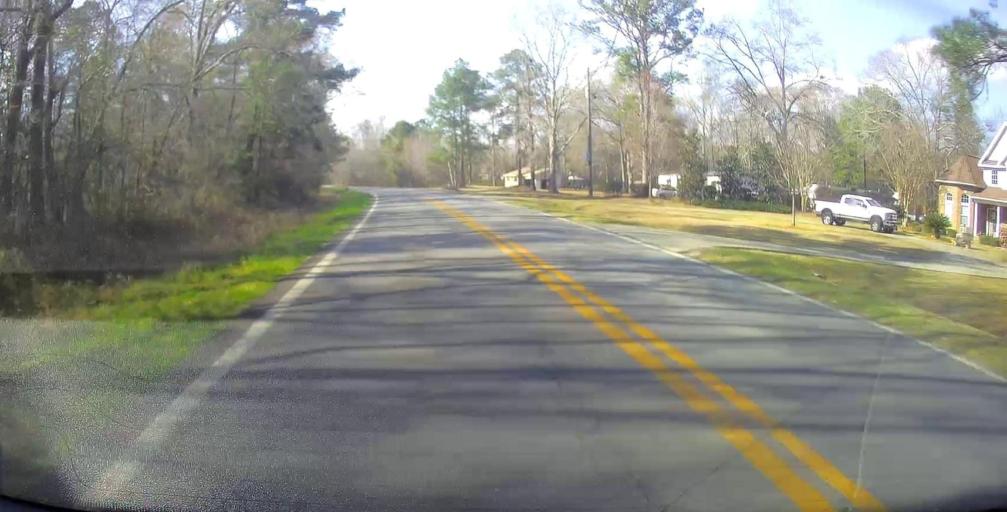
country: US
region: Georgia
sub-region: Laurens County
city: Dublin
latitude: 32.5548
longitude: -82.9954
